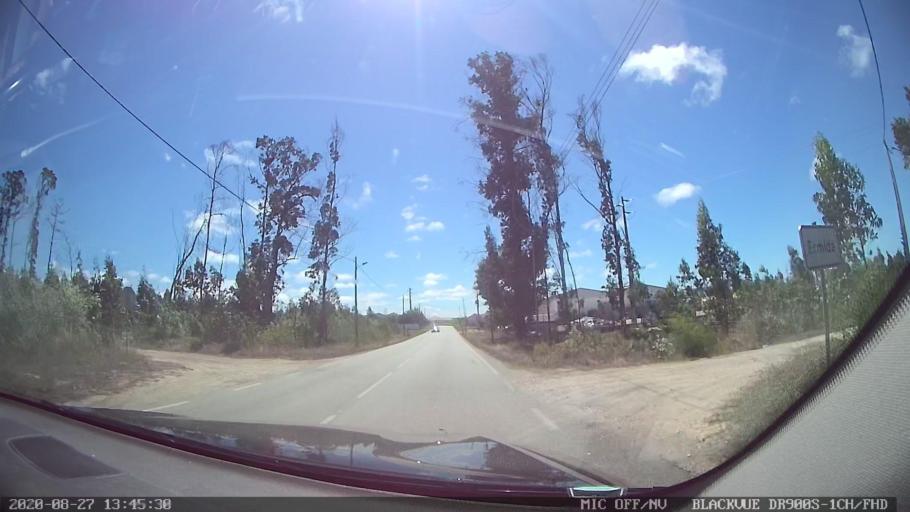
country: PT
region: Coimbra
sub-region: Mira
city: Mira
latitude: 40.4039
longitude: -8.7354
